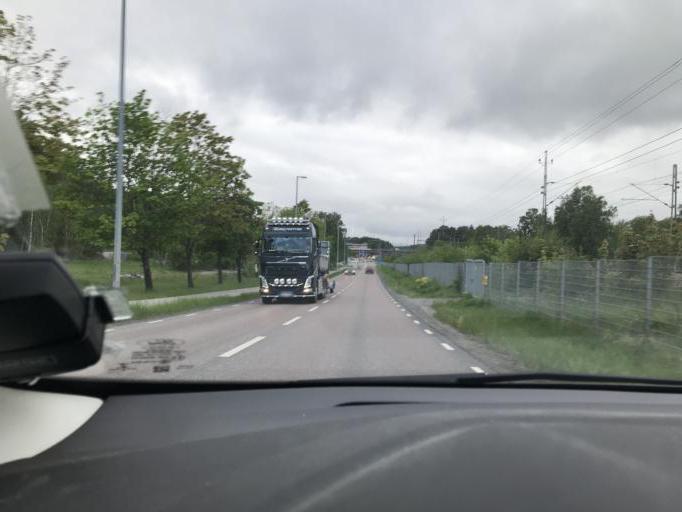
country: SE
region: Stockholm
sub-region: Botkyrka Kommun
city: Tumba
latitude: 59.1993
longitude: 17.8517
